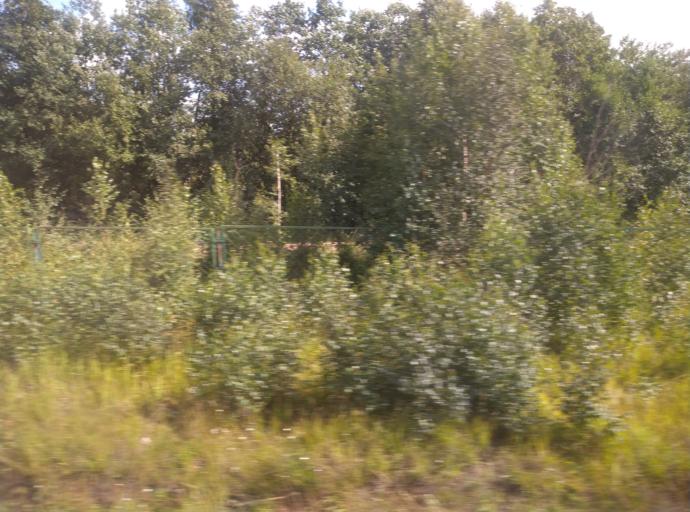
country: RU
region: Leningrad
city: Krasnyy Bor
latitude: 59.6794
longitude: 30.7027
